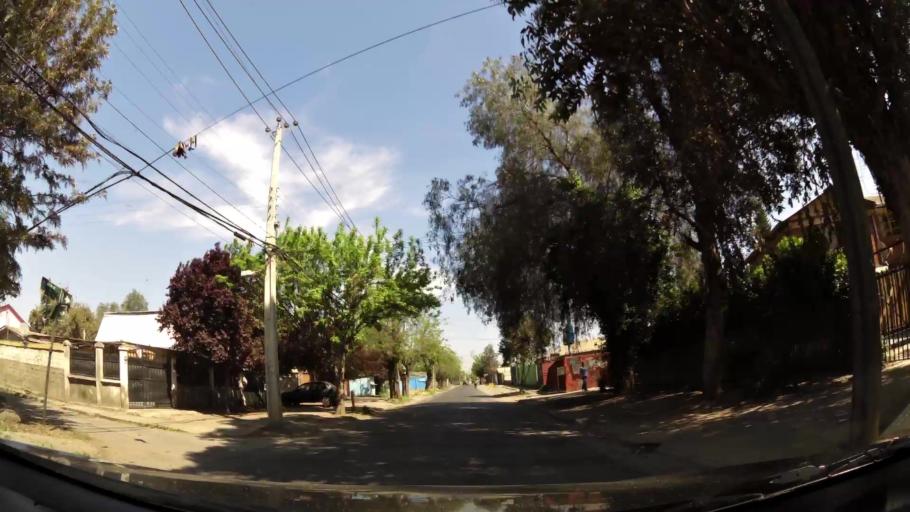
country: CL
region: Santiago Metropolitan
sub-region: Provincia de Santiago
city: Lo Prado
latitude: -33.4037
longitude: -70.7155
